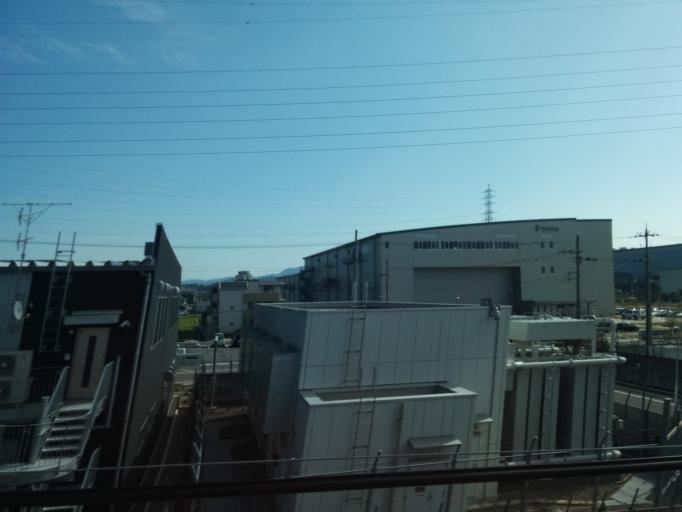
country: JP
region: Shiga Prefecture
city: Kusatsu
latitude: 35.0326
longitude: 135.9929
